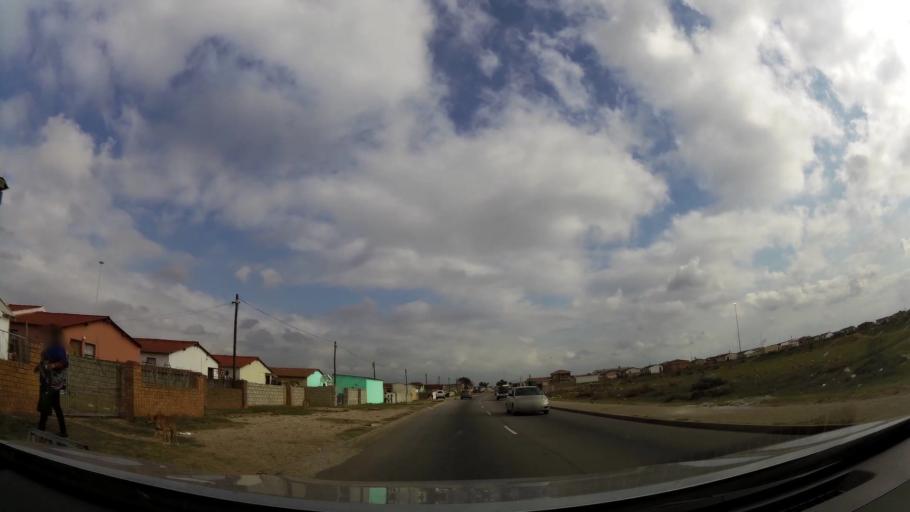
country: ZA
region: Eastern Cape
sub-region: Nelson Mandela Bay Metropolitan Municipality
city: Port Elizabeth
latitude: -33.8149
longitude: 25.5879
